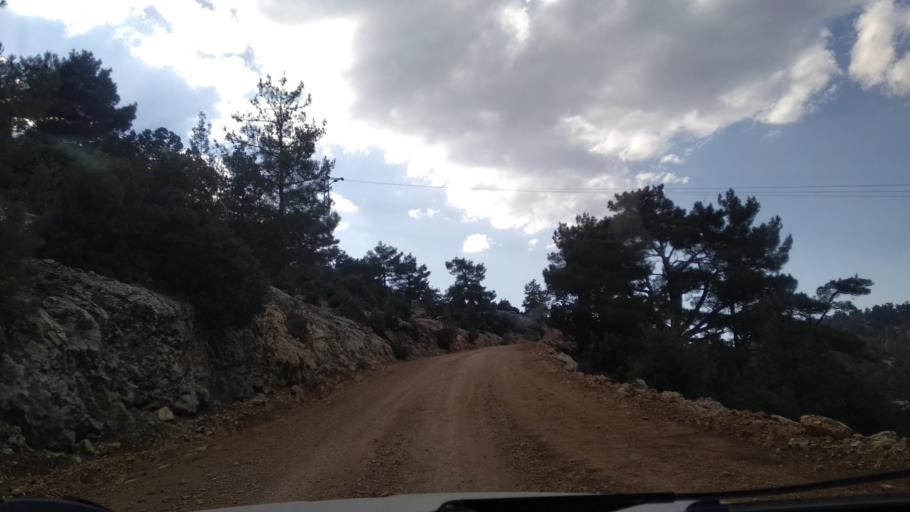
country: TR
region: Mersin
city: Sarikavak
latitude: 36.5987
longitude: 33.7038
